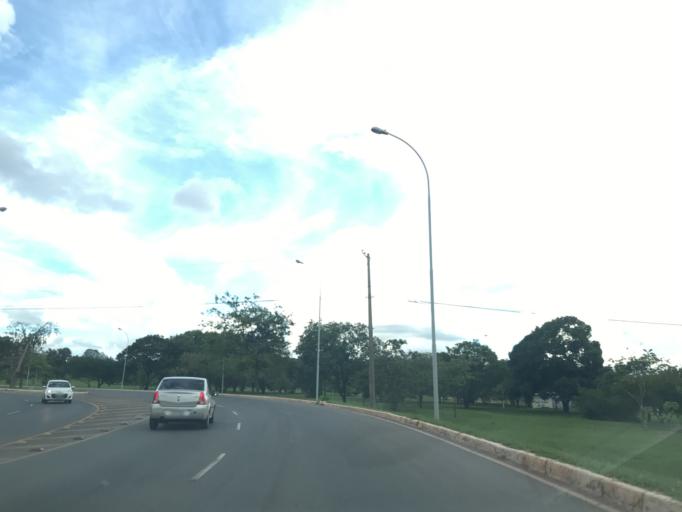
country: BR
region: Federal District
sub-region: Brasilia
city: Brasilia
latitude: -15.8113
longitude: -47.9264
